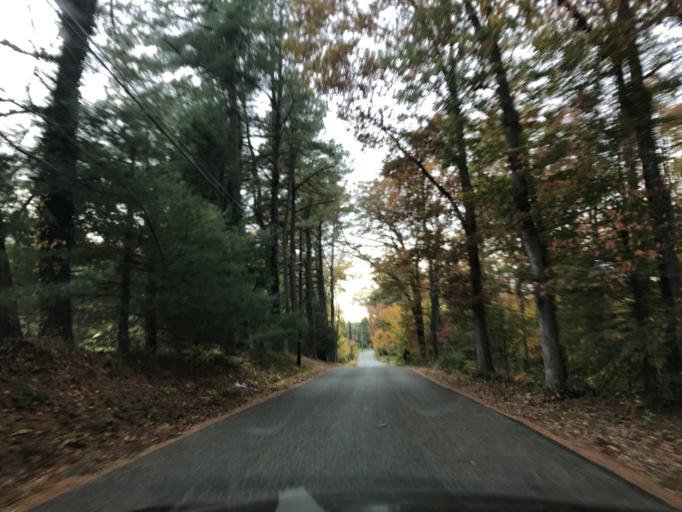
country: US
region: Maryland
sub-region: Harford County
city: Pleasant Hills
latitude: 39.4858
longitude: -76.3682
